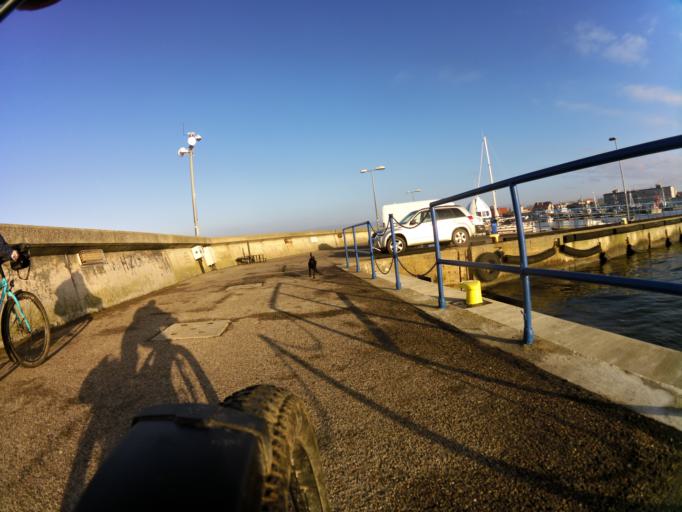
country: PL
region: Pomeranian Voivodeship
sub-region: Powiat pucki
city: Hel
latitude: 54.6013
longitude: 18.7991
